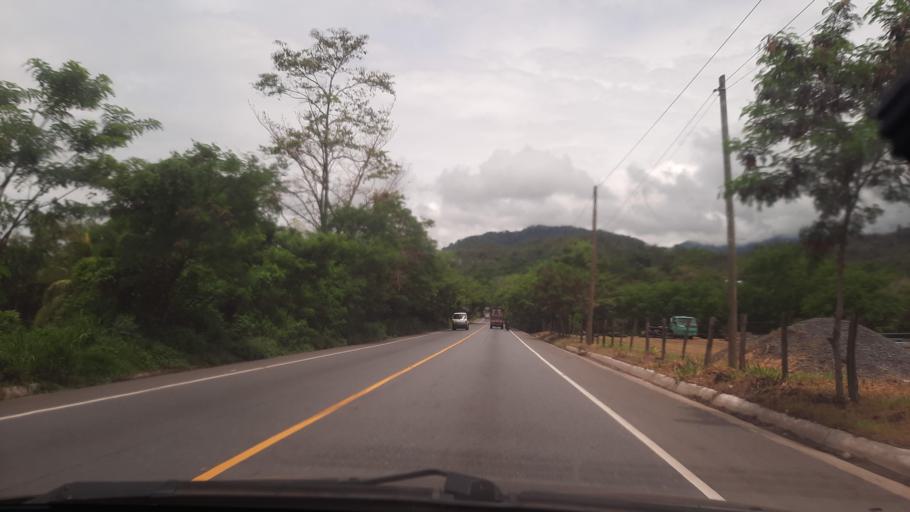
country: GT
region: Izabal
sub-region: Municipio de Los Amates
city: Los Amates
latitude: 15.2162
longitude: -89.2308
